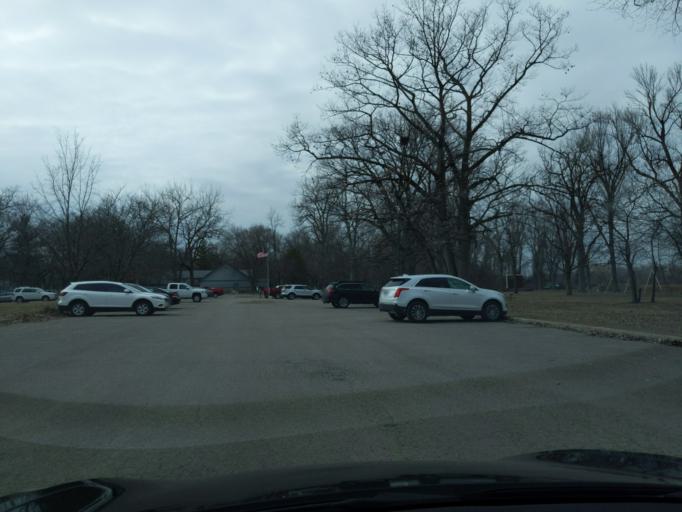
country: US
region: Michigan
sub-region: Bay County
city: Bay City
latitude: 43.6693
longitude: -83.9097
